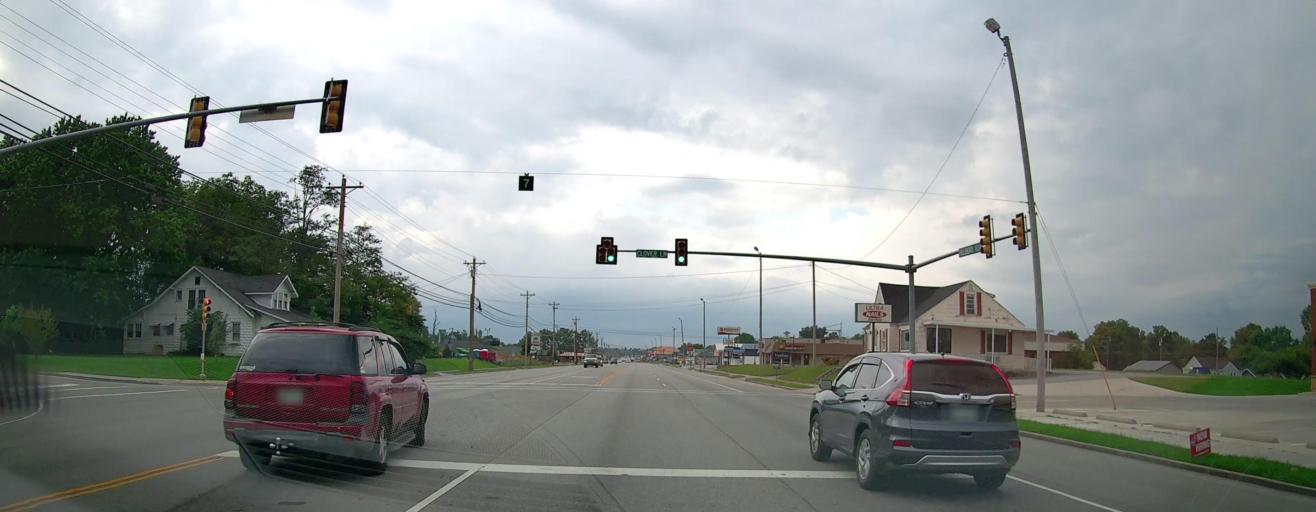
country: US
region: Tennessee
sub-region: Coffee County
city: Manchester
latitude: 35.4689
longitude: -86.0725
